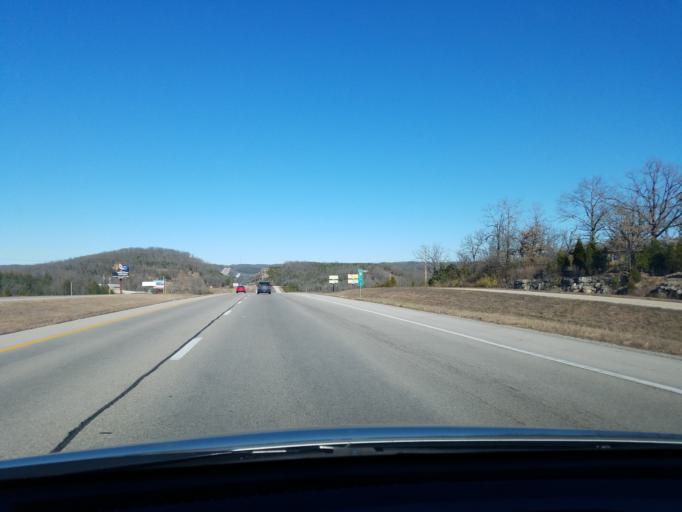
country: US
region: Missouri
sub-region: Taney County
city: Merriam Woods
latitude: 36.7525
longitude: -93.2226
